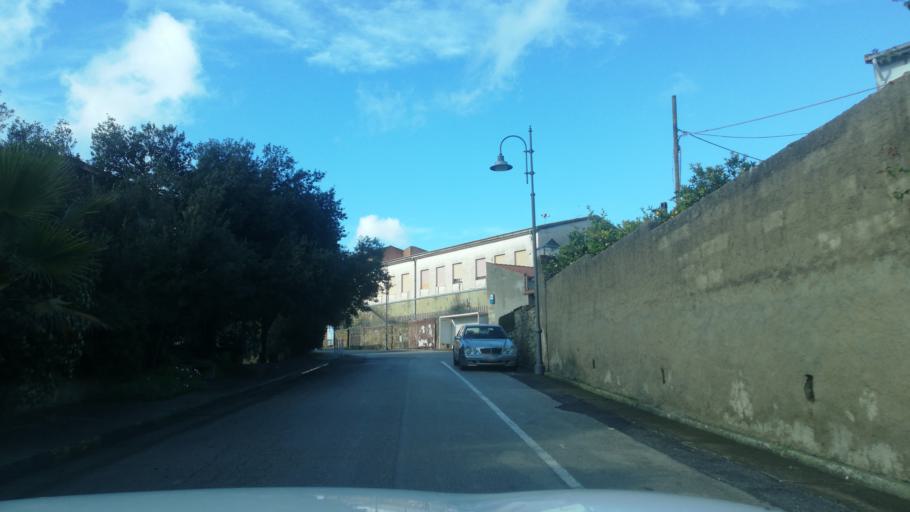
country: IT
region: Sardinia
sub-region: Provincia di Medio Campidano
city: Villanovaforru
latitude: 39.6312
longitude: 8.8727
